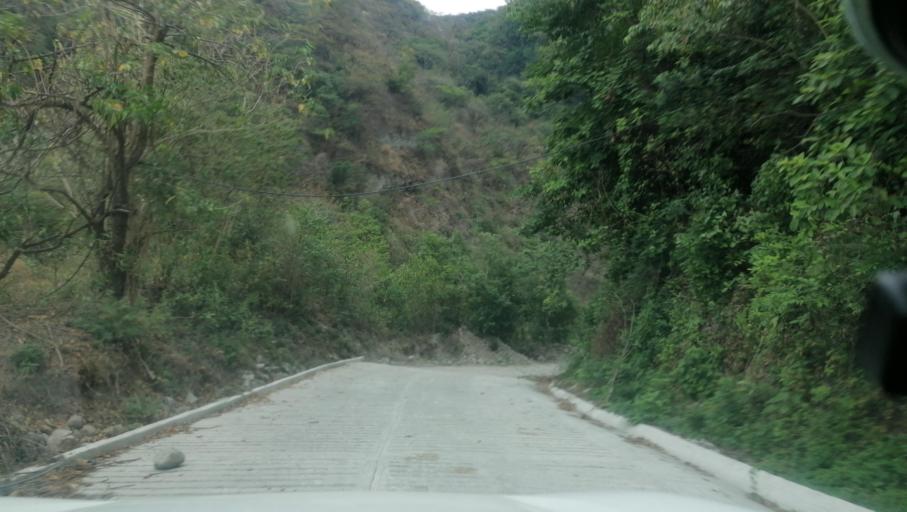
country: MX
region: Chiapas
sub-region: Cacahoatan
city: Benito Juarez
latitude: 15.1660
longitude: -92.1792
